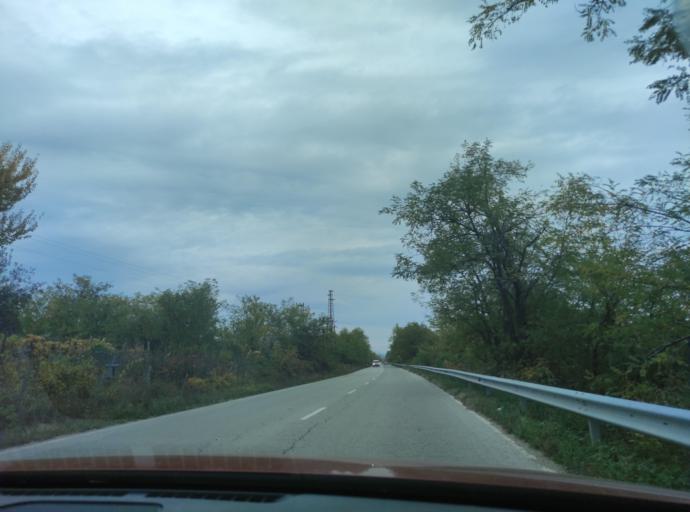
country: BG
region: Montana
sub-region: Obshtina Berkovitsa
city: Berkovitsa
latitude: 43.2117
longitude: 23.1595
